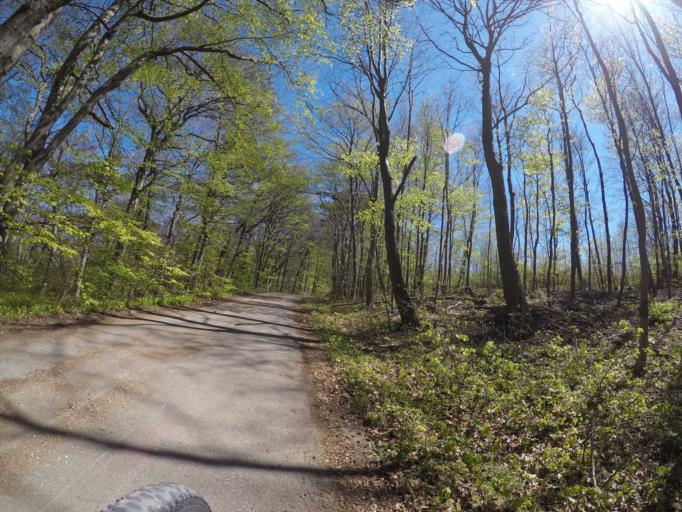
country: AT
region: Lower Austria
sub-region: Politischer Bezirk Modling
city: Gumpoldskirchen
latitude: 48.0527
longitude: 16.2499
